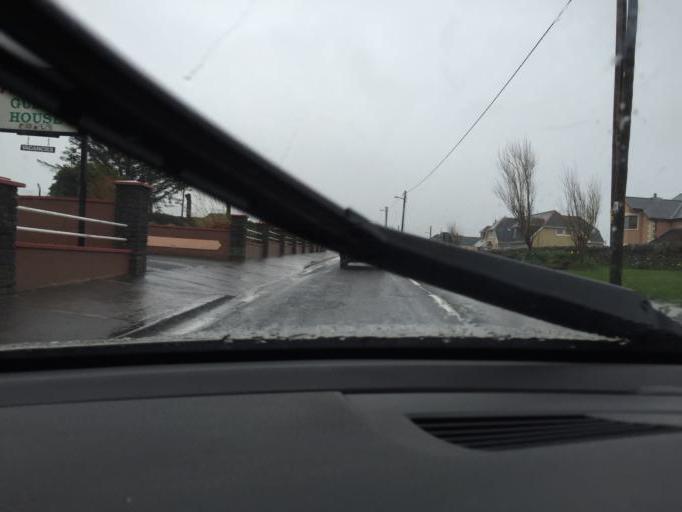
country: IE
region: Munster
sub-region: Ciarrai
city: Dingle
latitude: 52.1376
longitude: -10.2696
